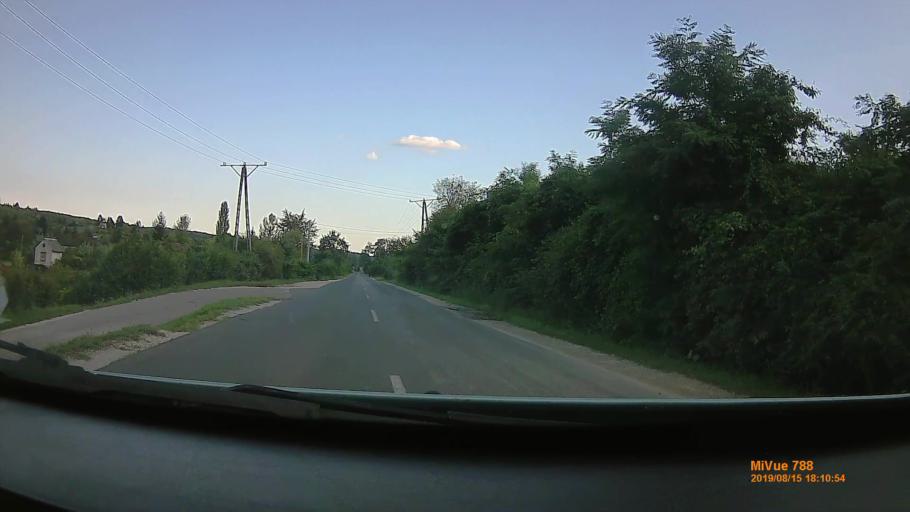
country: HU
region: Borsod-Abauj-Zemplen
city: Sajobabony
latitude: 48.1289
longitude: 20.7100
